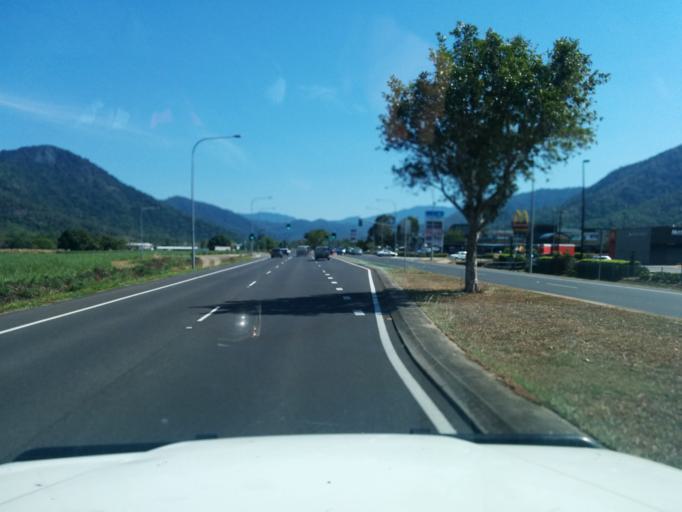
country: AU
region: Queensland
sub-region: Cairns
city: Redlynch
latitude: -16.8941
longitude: 145.7004
